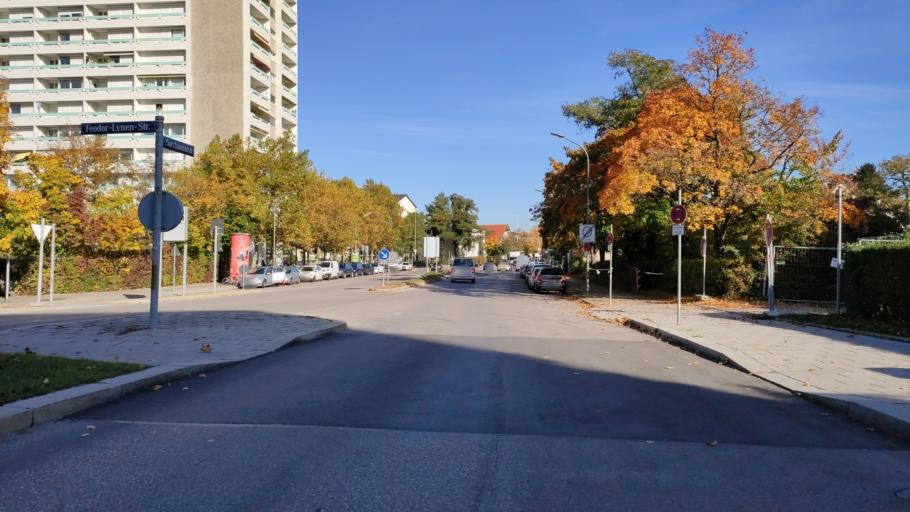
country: DE
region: Bavaria
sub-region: Upper Bavaria
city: Neuried
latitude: 48.1131
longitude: 11.4749
